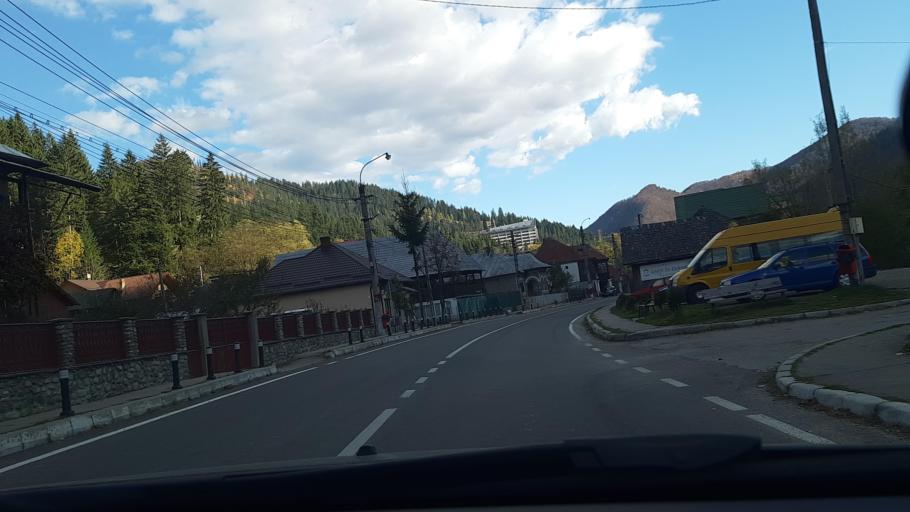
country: RO
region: Valcea
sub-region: Comuna Voineasa
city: Voineasa
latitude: 45.4196
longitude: 23.9564
